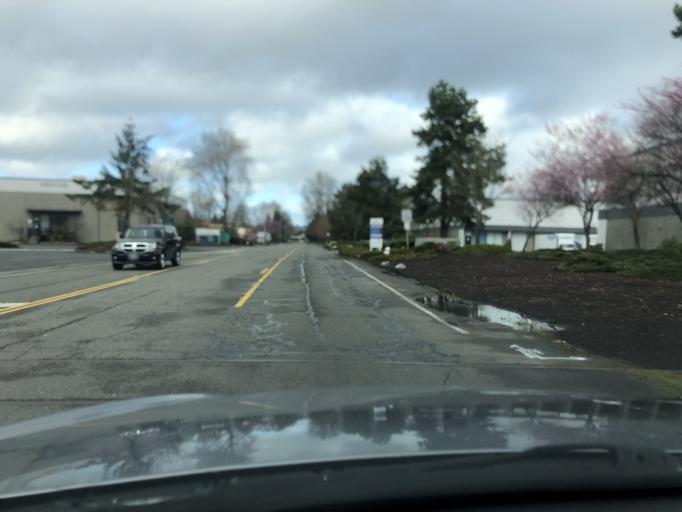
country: US
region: Washington
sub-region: King County
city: Tukwila
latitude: 47.4356
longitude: -122.2439
